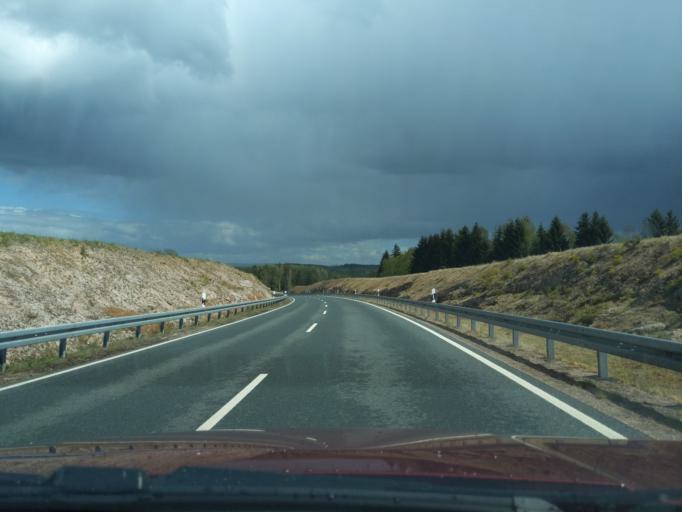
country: DE
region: Saxony
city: Stutzengrun
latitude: 50.5513
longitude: 12.5648
